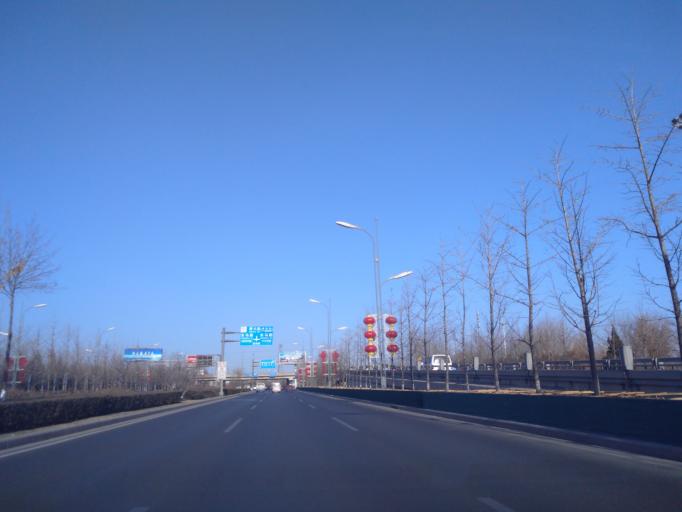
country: CN
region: Beijing
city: Jiugong
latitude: 39.8116
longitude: 116.4879
